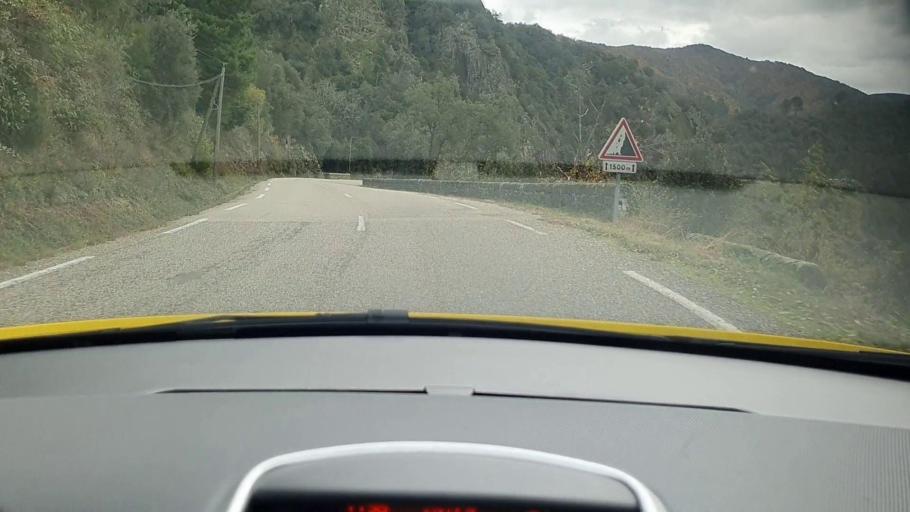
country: FR
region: Languedoc-Roussillon
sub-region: Departement du Gard
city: Lasalle
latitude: 44.1047
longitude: 3.8006
